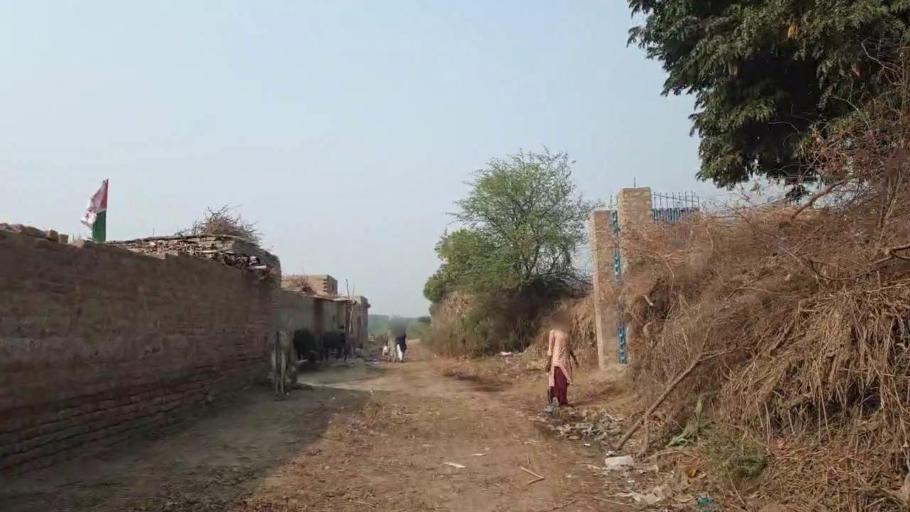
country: PK
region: Sindh
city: Tando Muhammad Khan
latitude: 25.2010
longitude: 68.5643
